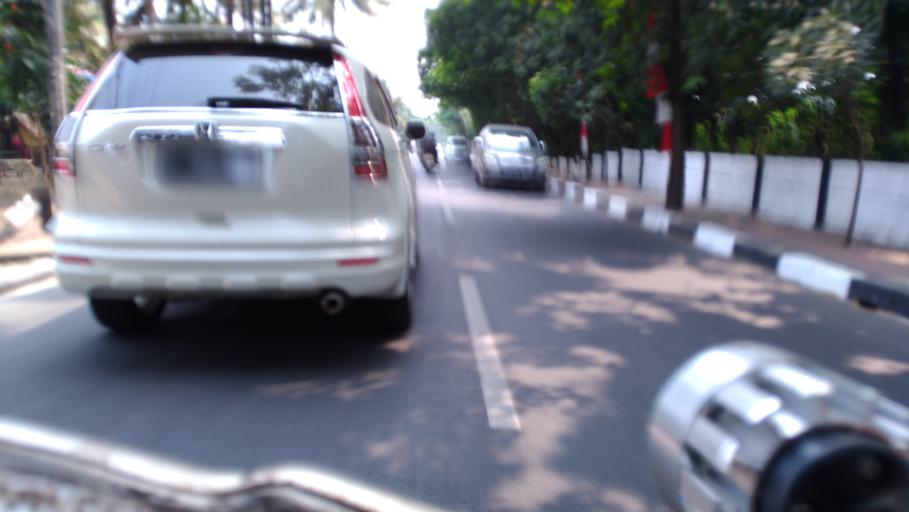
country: ID
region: West Java
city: Cileungsir
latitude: -6.3341
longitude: 106.8872
